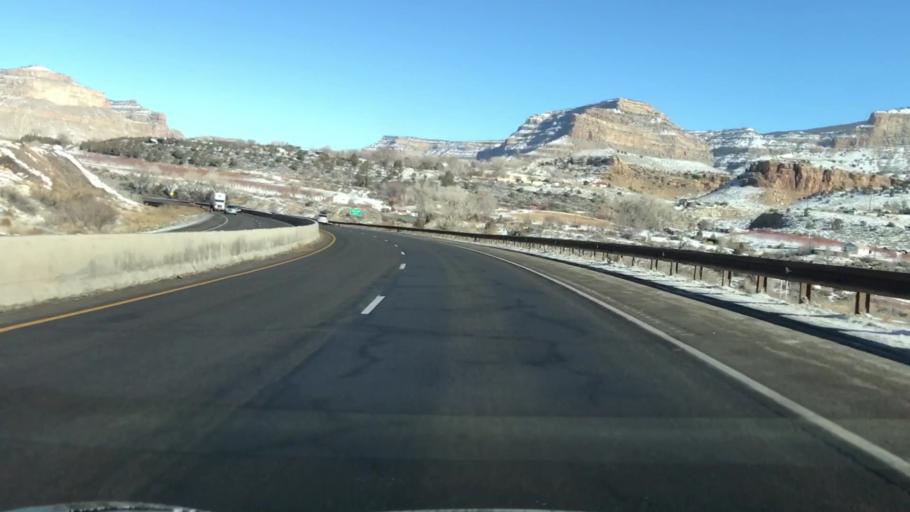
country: US
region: Colorado
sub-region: Mesa County
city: Palisade
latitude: 39.1209
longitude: -108.3248
